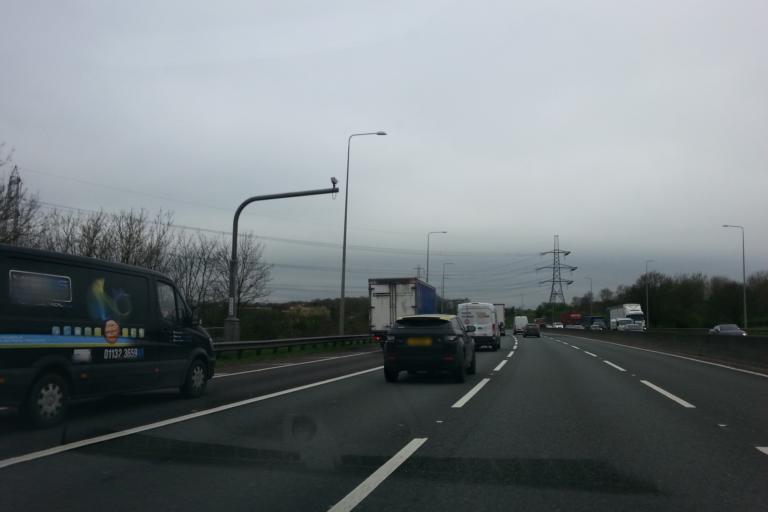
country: GB
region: England
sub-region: Kirklees
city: Cleckheaton
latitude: 53.7453
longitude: -1.7073
